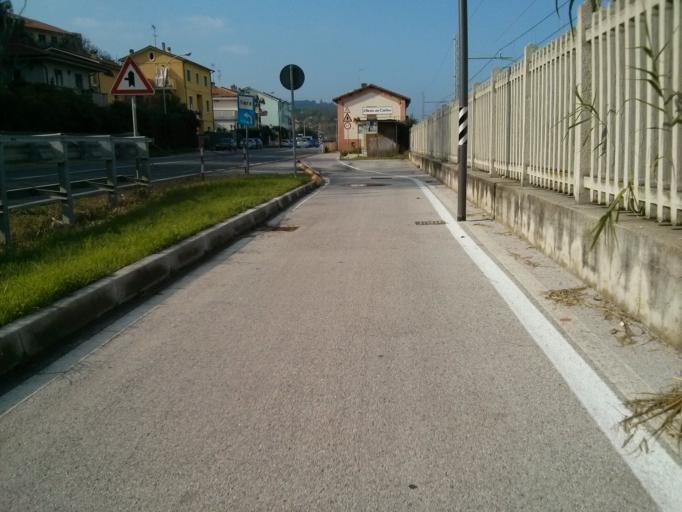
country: IT
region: The Marches
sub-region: Provincia di Pesaro e Urbino
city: Fenile
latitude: 43.8786
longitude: 12.9655
